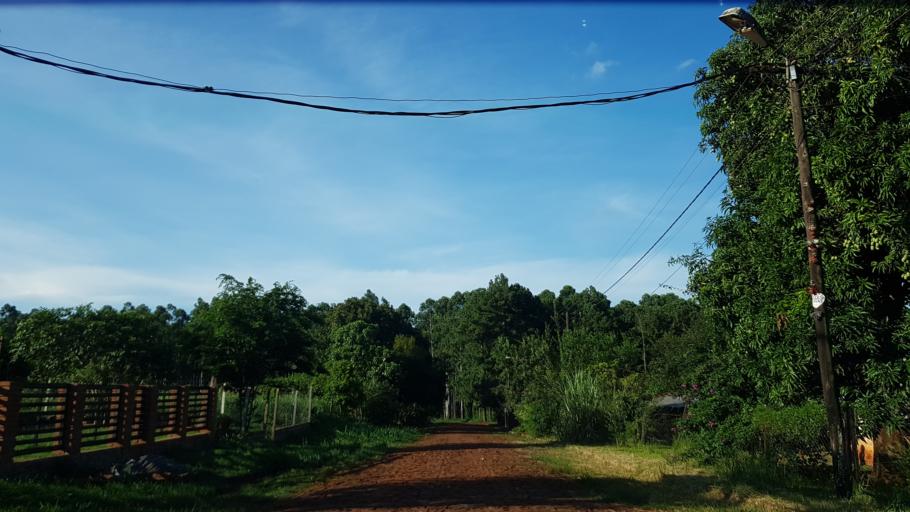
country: AR
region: Misiones
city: Puerto Libertad
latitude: -25.9160
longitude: -54.5893
